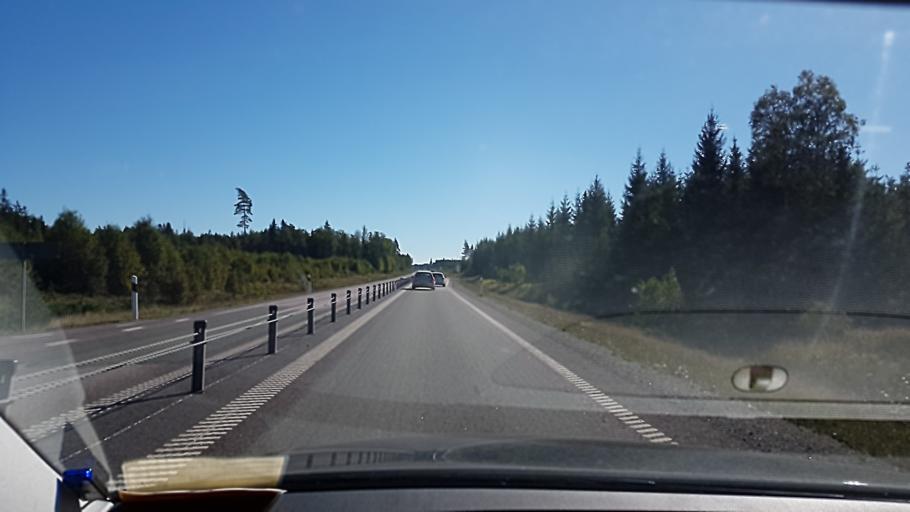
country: SE
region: Kalmar
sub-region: Emmaboda Kommun
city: Emmaboda
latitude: 56.7314
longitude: 15.5447
